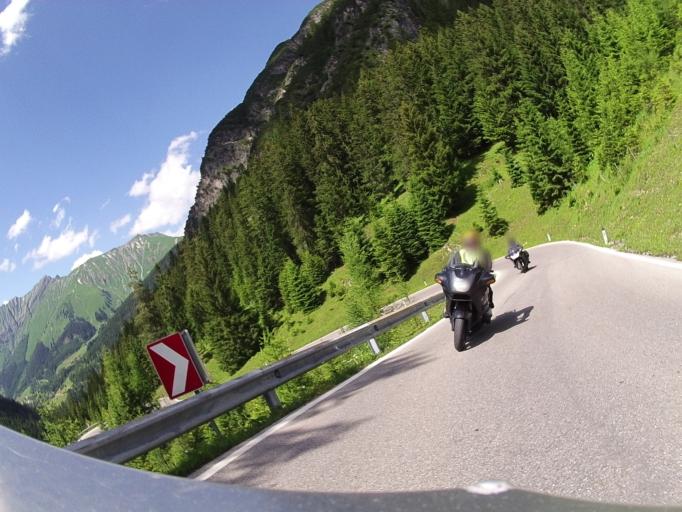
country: AT
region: Tyrol
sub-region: Politischer Bezirk Reutte
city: Gramais
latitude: 47.2868
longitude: 10.6080
